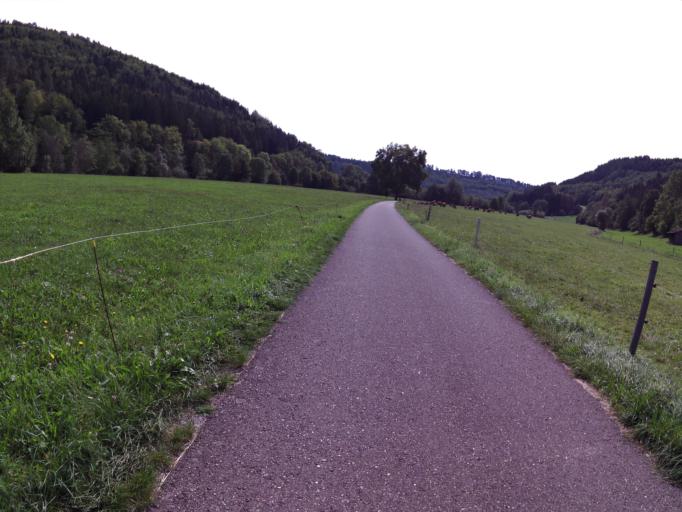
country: DE
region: Baden-Wuerttemberg
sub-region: Freiburg Region
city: Sulz am Neckar
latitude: 48.4074
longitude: 8.6394
